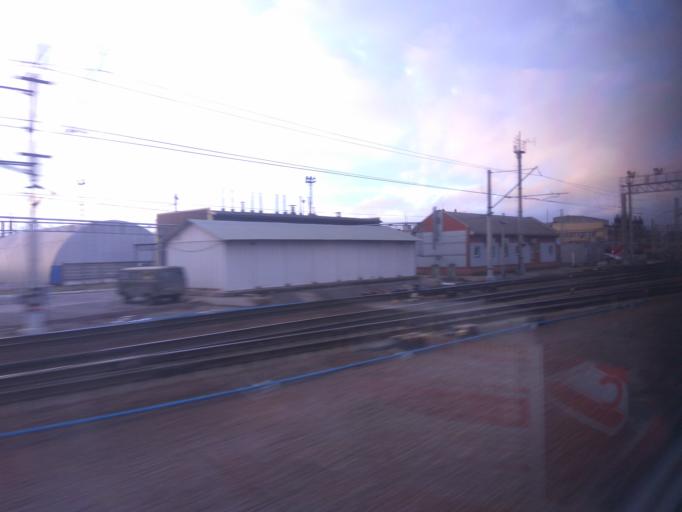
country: RU
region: St.-Petersburg
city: Centralniy
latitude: 59.9148
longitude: 30.3672
